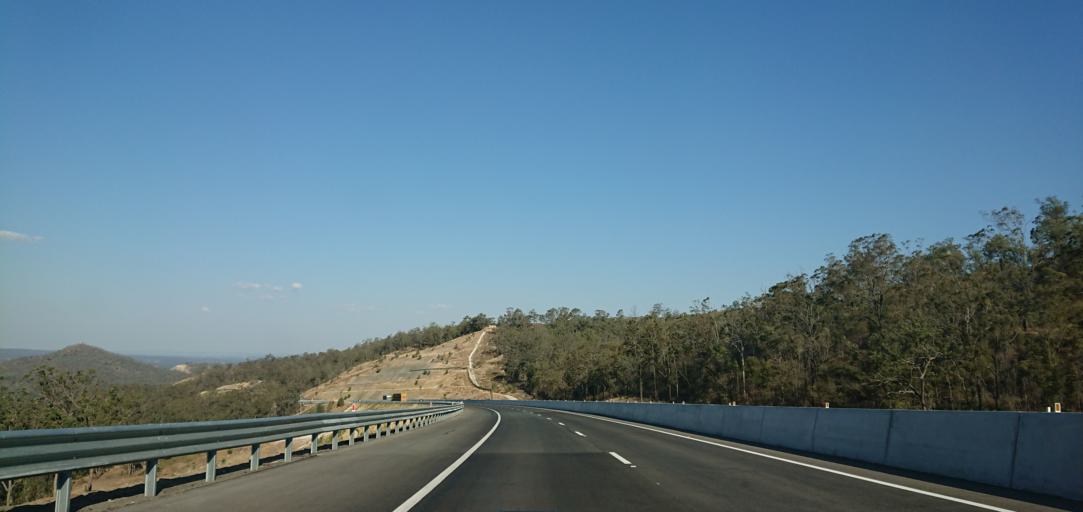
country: AU
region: Queensland
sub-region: Toowoomba
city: East Toowoomba
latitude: -27.5050
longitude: 151.9954
